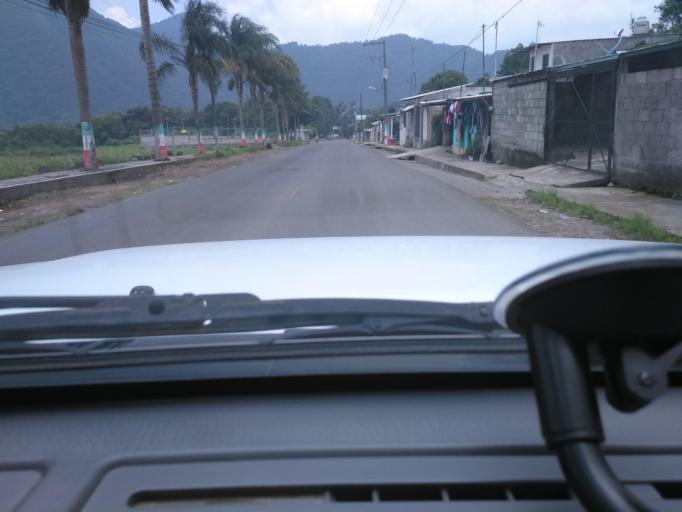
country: MX
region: Veracruz
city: Atzacan
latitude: 18.8912
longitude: -97.0904
